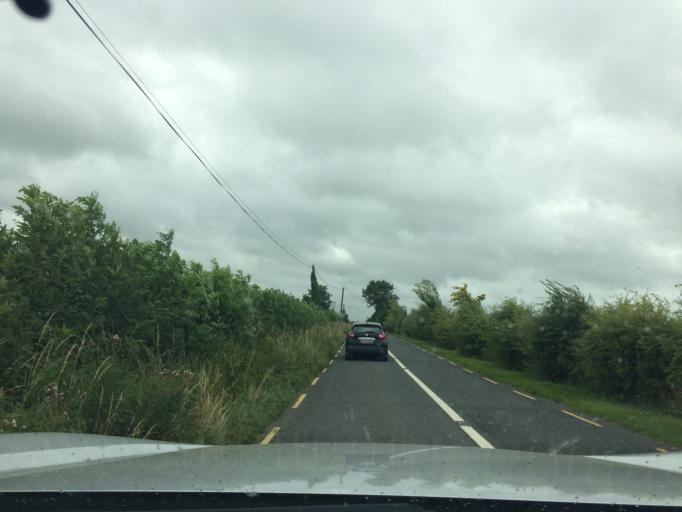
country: IE
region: Munster
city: Thurles
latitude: 52.6179
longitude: -7.8803
